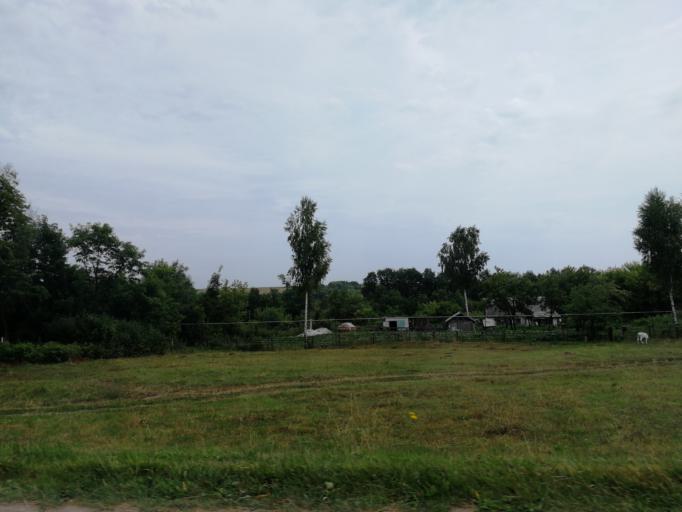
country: RU
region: Tula
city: Zhdankovskiy
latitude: 53.7038
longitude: 38.1568
